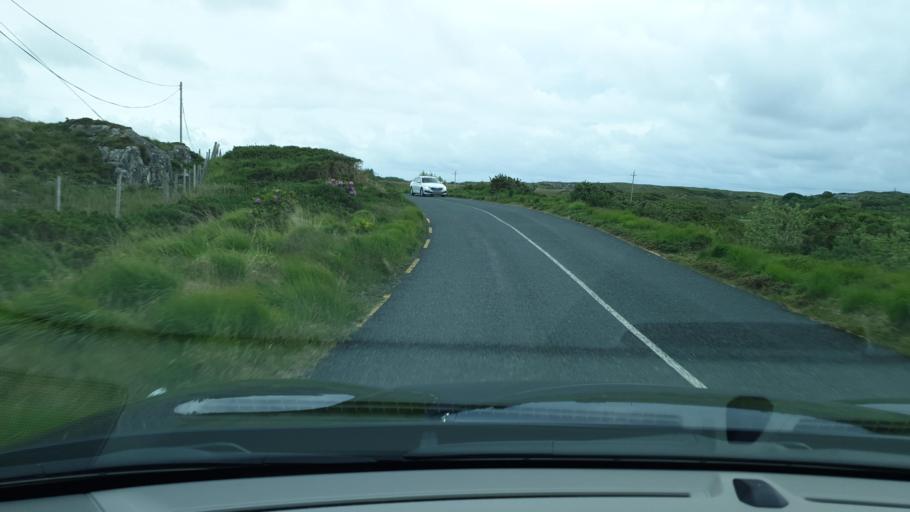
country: IE
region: Connaught
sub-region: County Galway
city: Clifden
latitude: 53.4449
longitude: -9.8780
